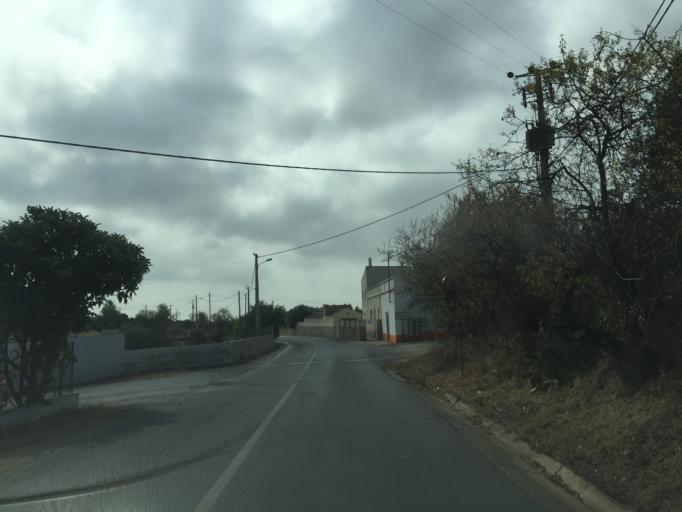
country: PT
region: Faro
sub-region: Olhao
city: Olhao
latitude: 37.0730
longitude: -7.8864
